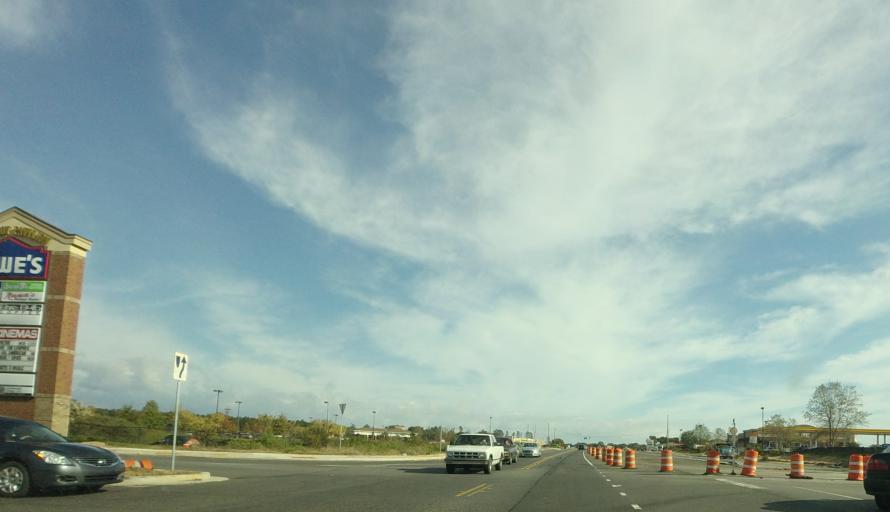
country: US
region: Georgia
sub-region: Houston County
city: Centerville
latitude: 32.5485
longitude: -83.6929
